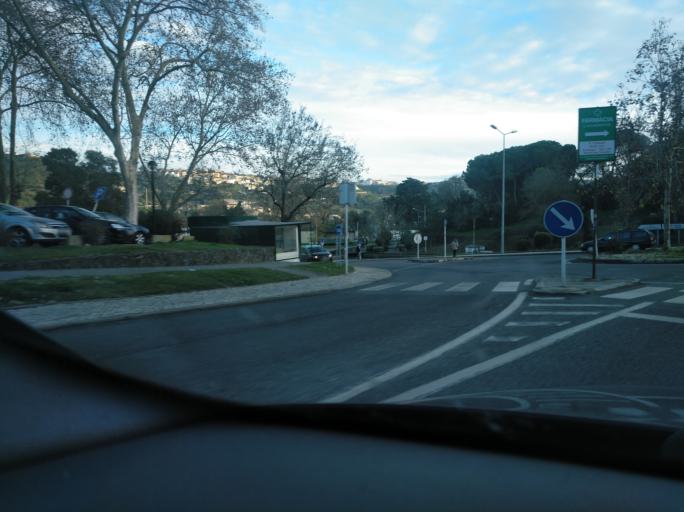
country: PT
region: Lisbon
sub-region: Odivelas
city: Povoa de Santo Adriao
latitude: 38.8133
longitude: -9.1575
